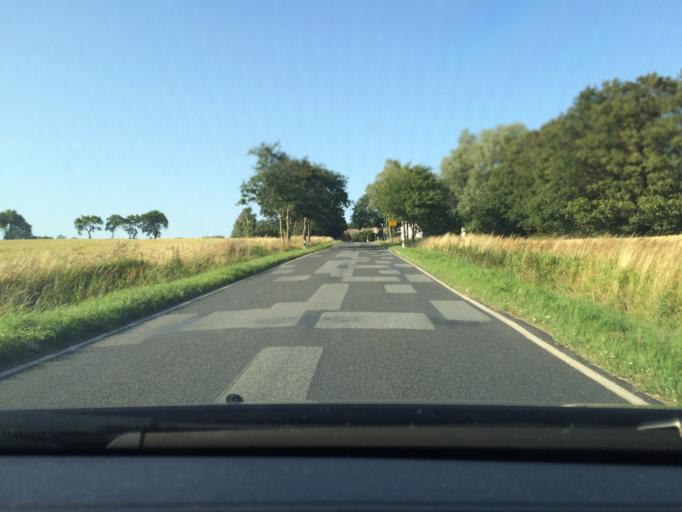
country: DE
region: Mecklenburg-Vorpommern
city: Altenpleen
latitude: 54.3841
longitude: 12.9435
